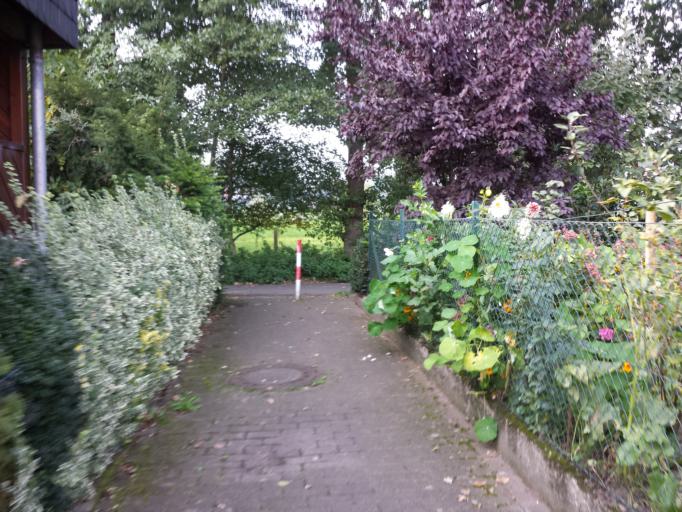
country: DE
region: North Rhine-Westphalia
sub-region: Regierungsbezirk Detmold
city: Guetersloh
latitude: 51.9111
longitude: 8.3525
